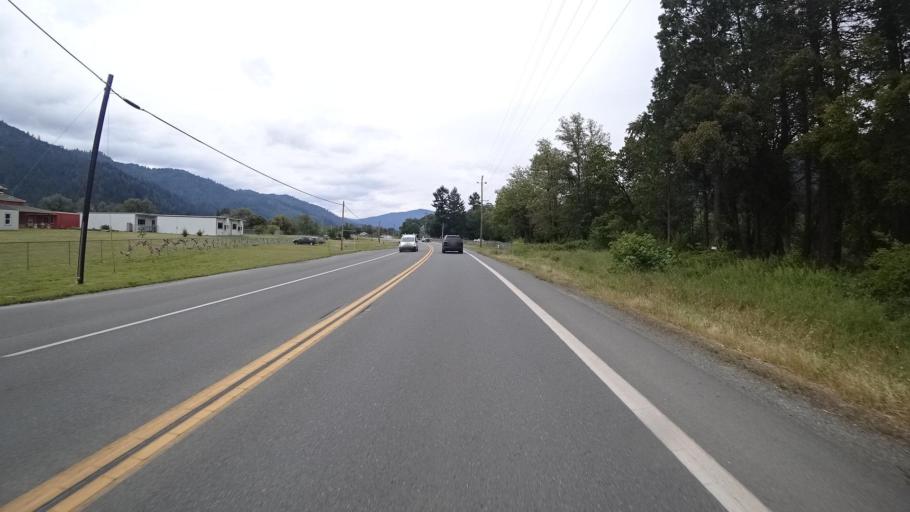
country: US
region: California
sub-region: Humboldt County
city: Willow Creek
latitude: 41.0508
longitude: -123.6747
